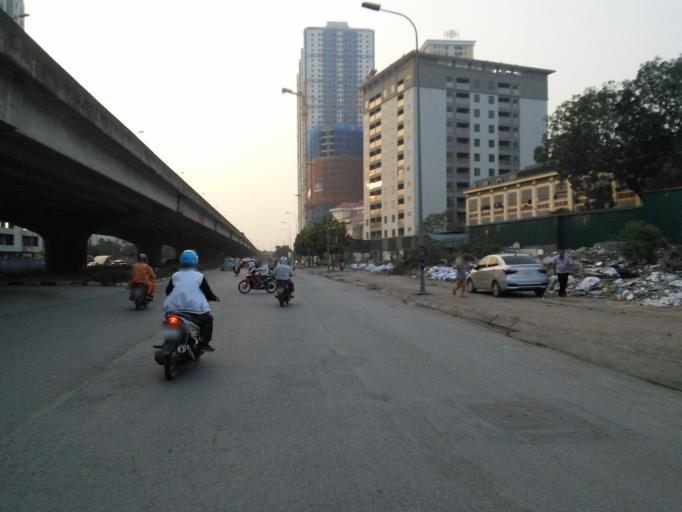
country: VN
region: Ha Noi
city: Van Dien
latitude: 20.9713
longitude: 105.8237
